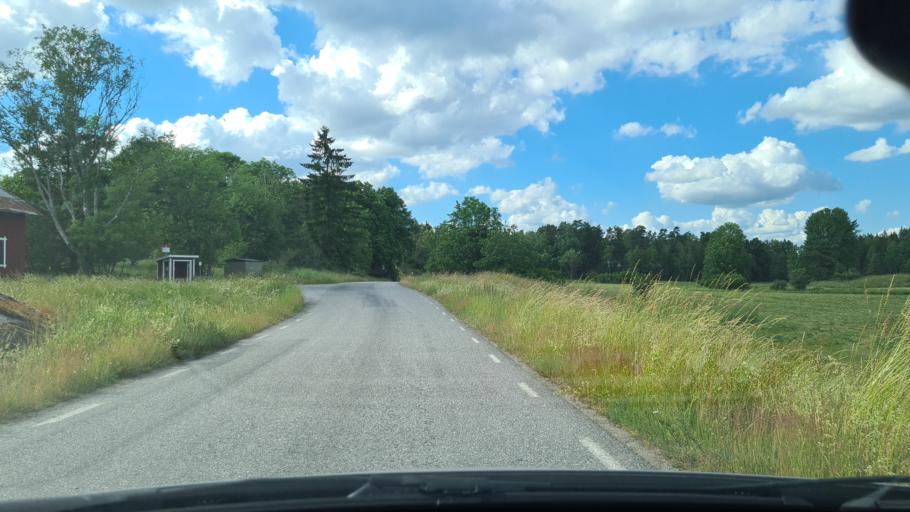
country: SE
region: Stockholm
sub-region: Varmdo Kommun
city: Mortnas
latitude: 59.4074
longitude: 18.4558
